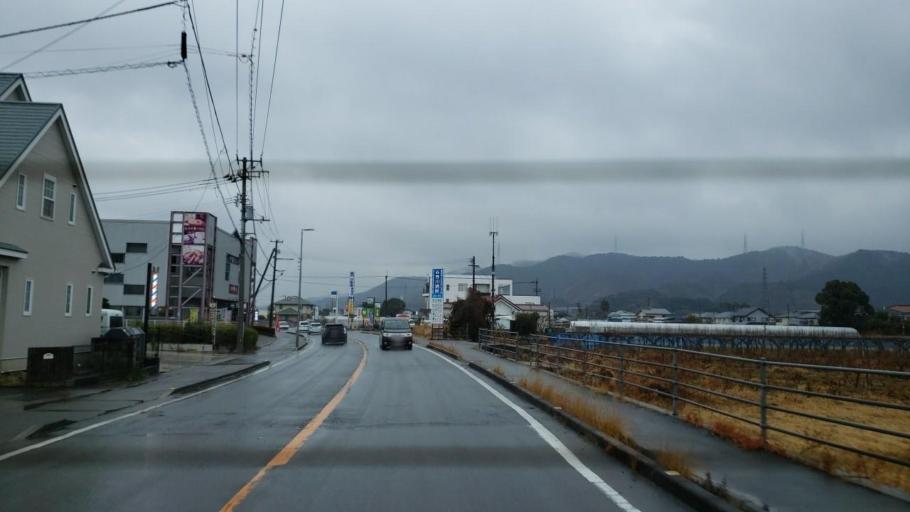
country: JP
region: Tokushima
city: Narutocho-mitsuishi
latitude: 34.1657
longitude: 134.5739
